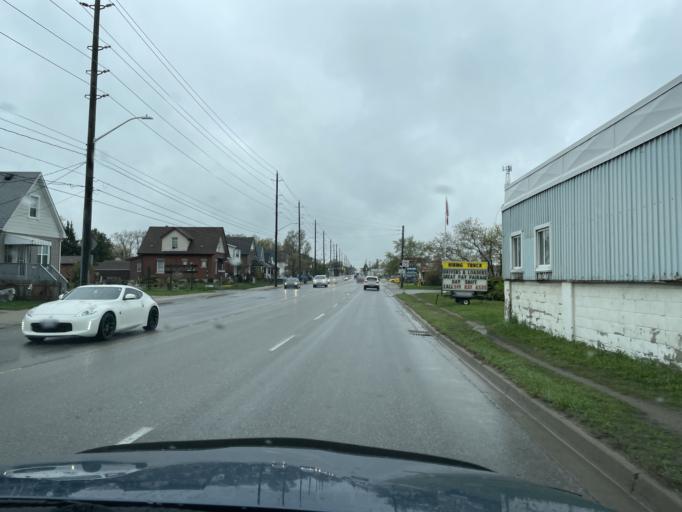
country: CA
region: Ontario
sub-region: Wellington County
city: Guelph
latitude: 43.5501
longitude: -80.2213
